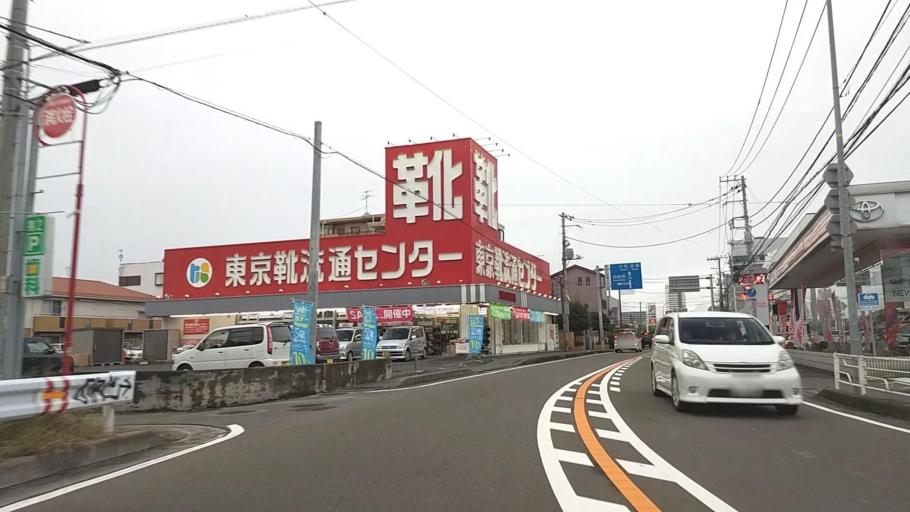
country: JP
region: Kanagawa
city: Atsugi
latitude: 35.4510
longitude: 139.3780
